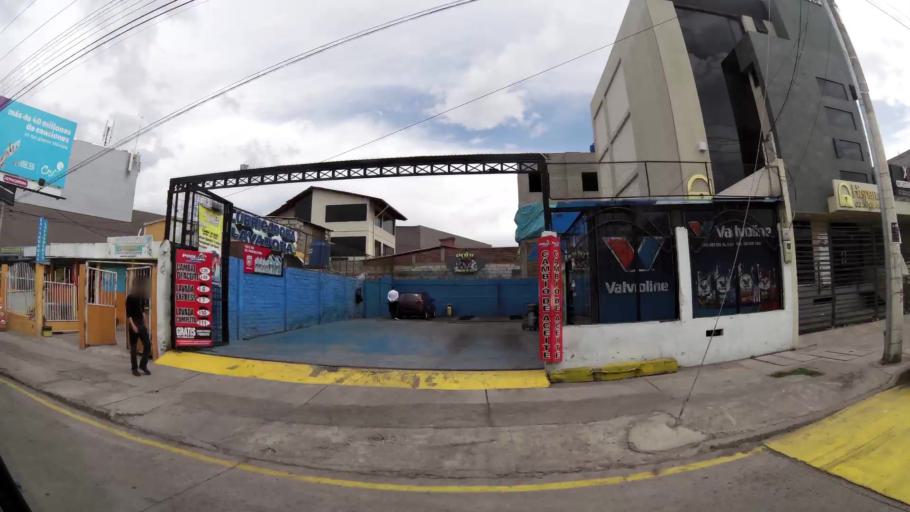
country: EC
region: Tungurahua
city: Ambato
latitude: -1.2648
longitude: -78.6292
